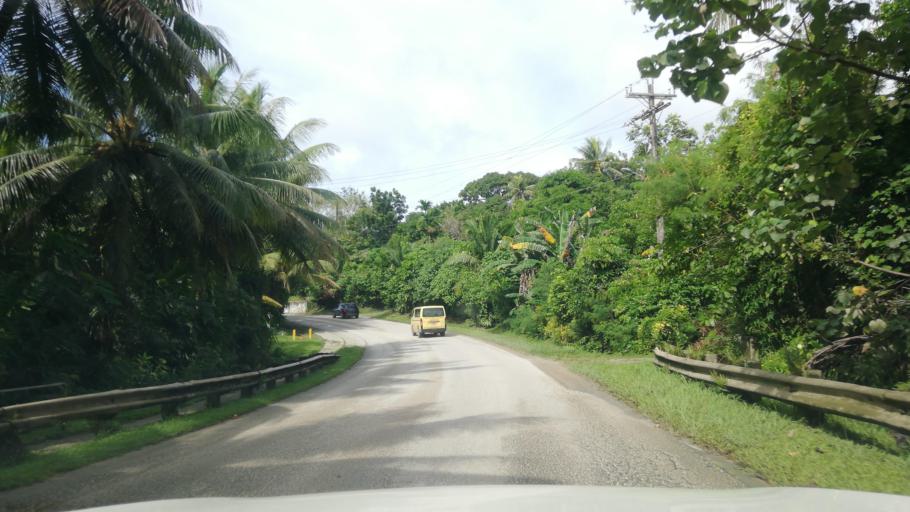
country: FM
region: Yap
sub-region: Weloy Municipality
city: Colonia
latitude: 9.5148
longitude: 138.1088
